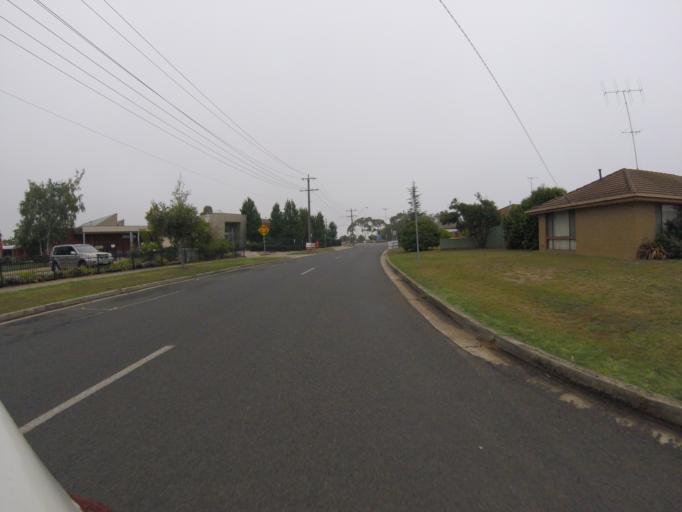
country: AU
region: Victoria
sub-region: Ballarat North
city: Newington
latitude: -37.5529
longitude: 143.7993
